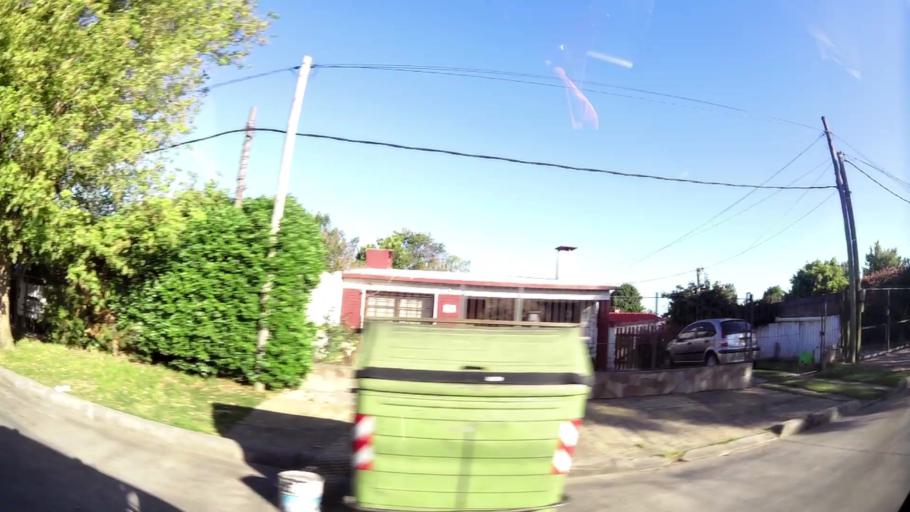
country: UY
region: Canelones
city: La Paz
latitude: -34.8317
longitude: -56.2049
